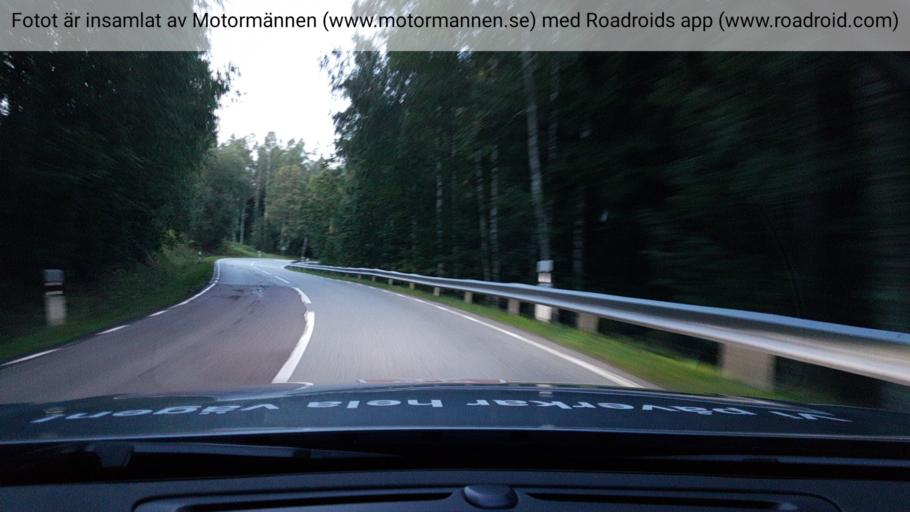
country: SE
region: OErebro
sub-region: Ljusnarsbergs Kommun
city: Kopparberg
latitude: 59.8529
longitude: 14.9988
